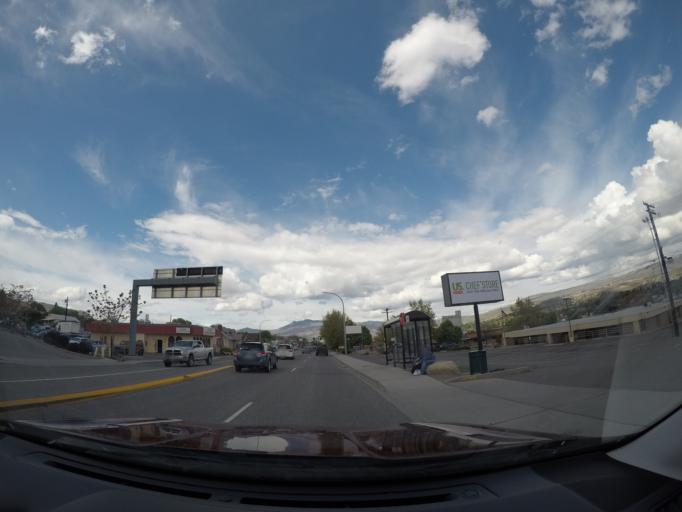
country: US
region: Washington
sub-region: Douglas County
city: East Wenatchee
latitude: 47.4118
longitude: -120.3038
